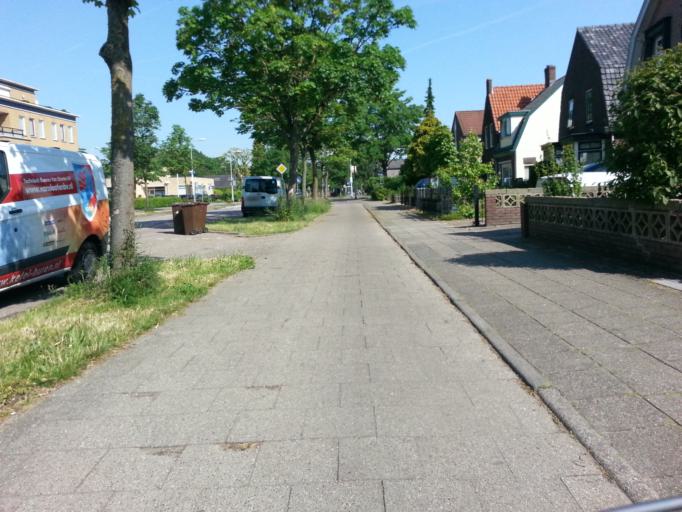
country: NL
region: Utrecht
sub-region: Gemeente Wijk bij Duurstede
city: Wijk bij Duurstede
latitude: 51.9774
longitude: 5.3447
